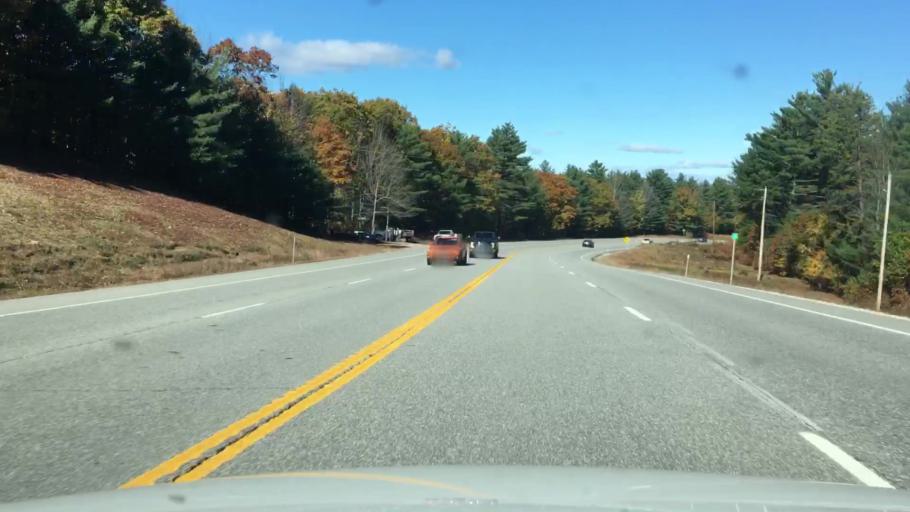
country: US
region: New Hampshire
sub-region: Carroll County
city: Ossipee
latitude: 43.6535
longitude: -71.0690
